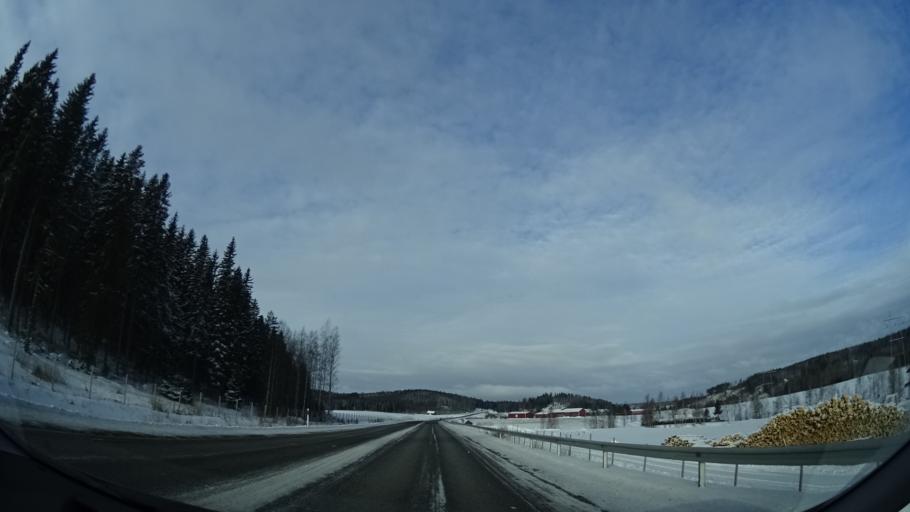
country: FI
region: Uusimaa
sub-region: Helsinki
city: Karkkila
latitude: 60.5716
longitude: 24.1597
